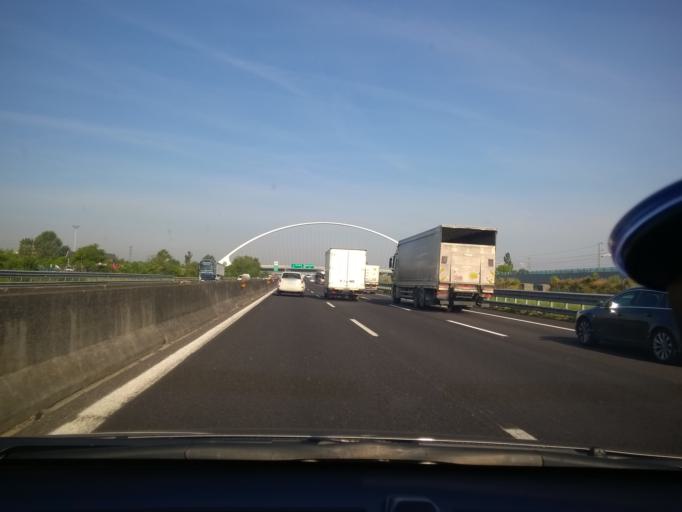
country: IT
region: Emilia-Romagna
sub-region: Provincia di Reggio Emilia
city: Reggio nell'Emilia
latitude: 44.7264
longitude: 10.6416
